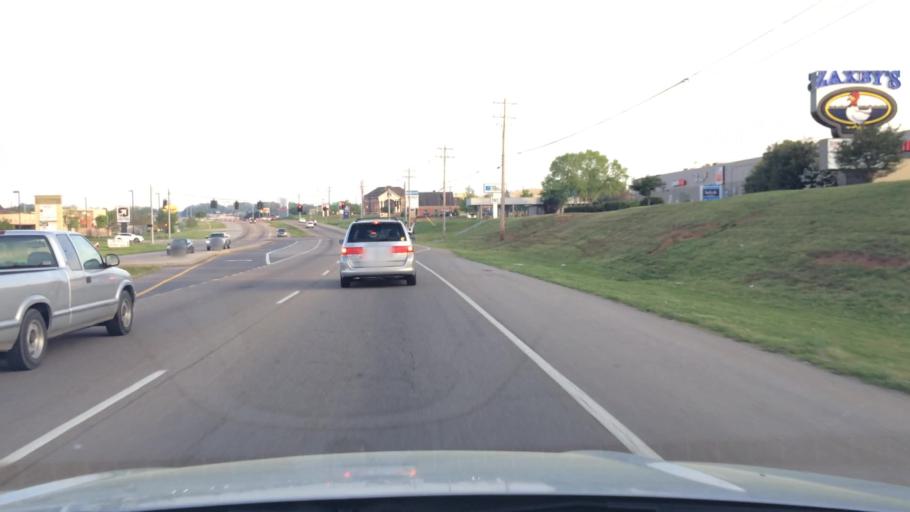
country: US
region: Tennessee
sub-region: Loudon County
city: Lenoir City
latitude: 35.8201
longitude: -84.2670
